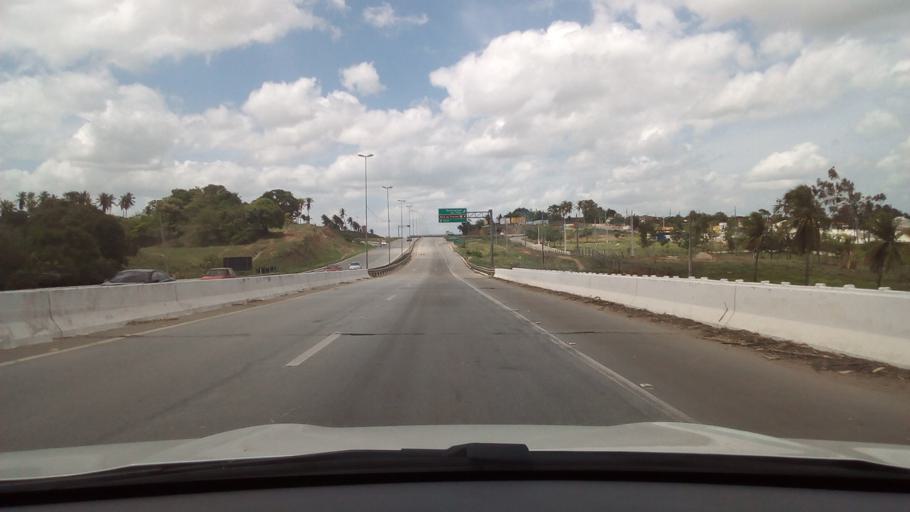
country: BR
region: Paraiba
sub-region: Mamanguape
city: Mamanguape
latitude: -6.8548
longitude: -35.1345
